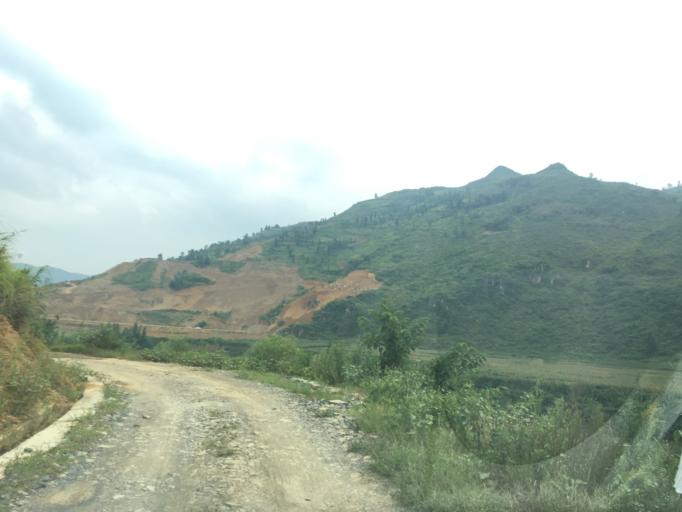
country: CN
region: Guangxi Zhuangzu Zizhiqu
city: Xinzhou
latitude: 25.1839
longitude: 105.7321
